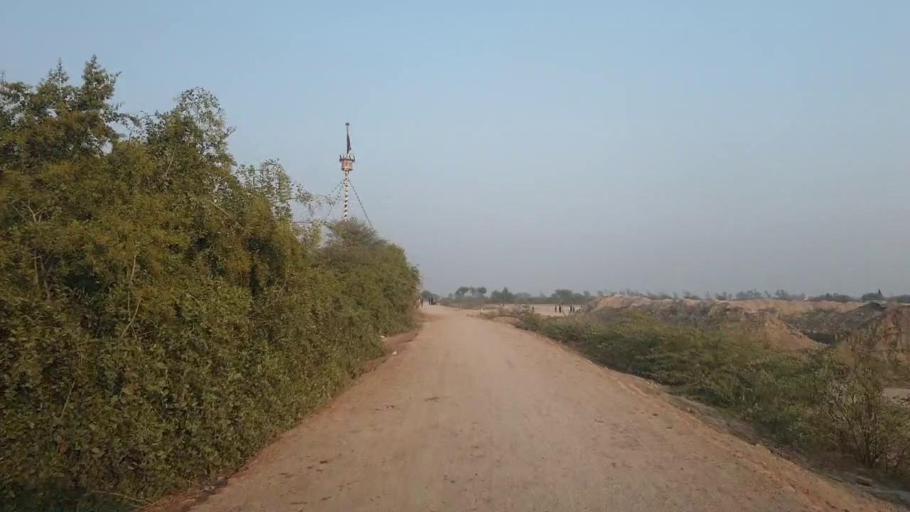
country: PK
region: Sindh
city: Bhit Shah
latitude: 25.7941
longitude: 68.4684
